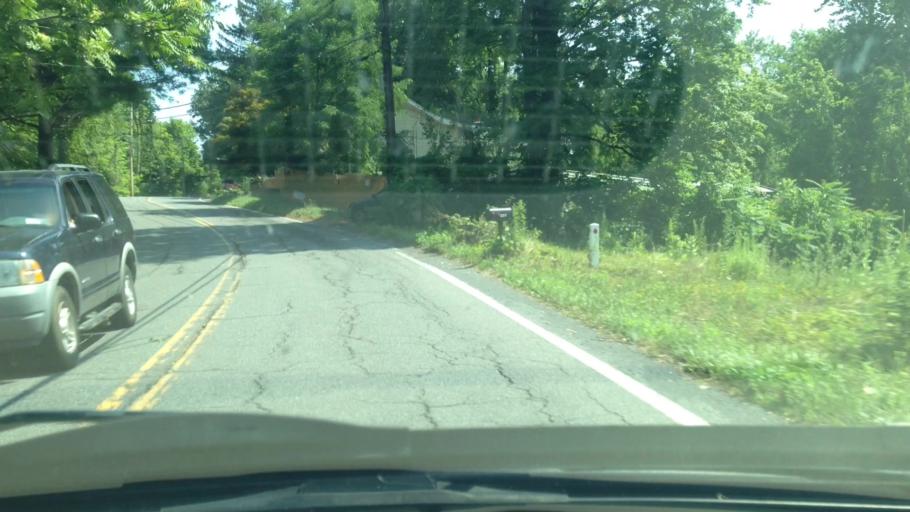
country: US
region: New York
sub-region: Ulster County
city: Kingston
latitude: 41.8998
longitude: -74.0088
